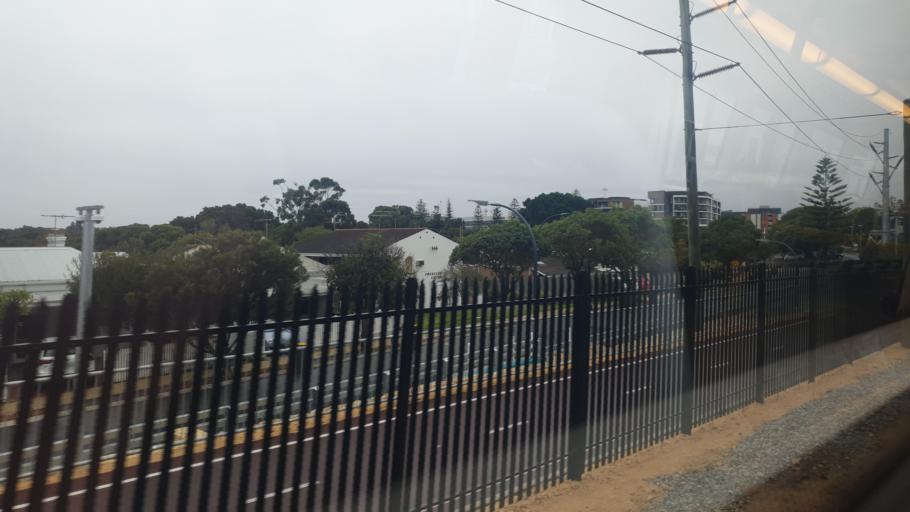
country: AU
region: Western Australia
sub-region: Claremont
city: Claremont
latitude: -31.9815
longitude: 115.7790
